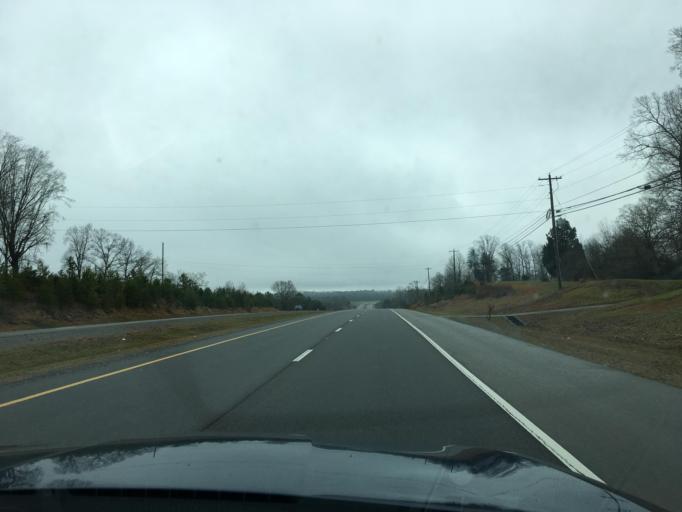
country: US
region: Tennessee
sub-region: McMinn County
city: Athens
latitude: 35.3965
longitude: -84.5712
